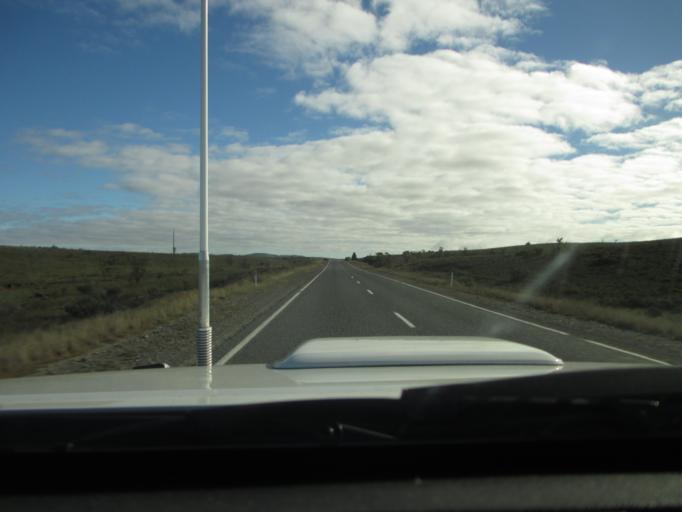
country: AU
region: South Australia
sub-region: Peterborough
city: Peterborough
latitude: -32.6090
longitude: 138.5701
